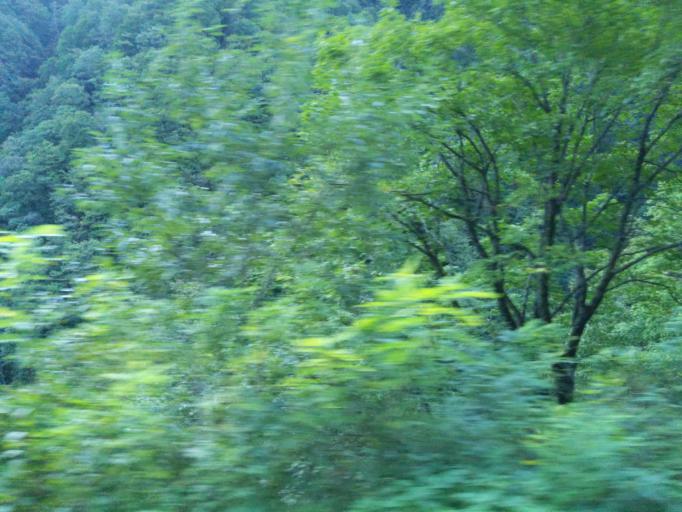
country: JP
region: Toyama
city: Kamiichi
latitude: 36.5182
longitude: 137.4492
